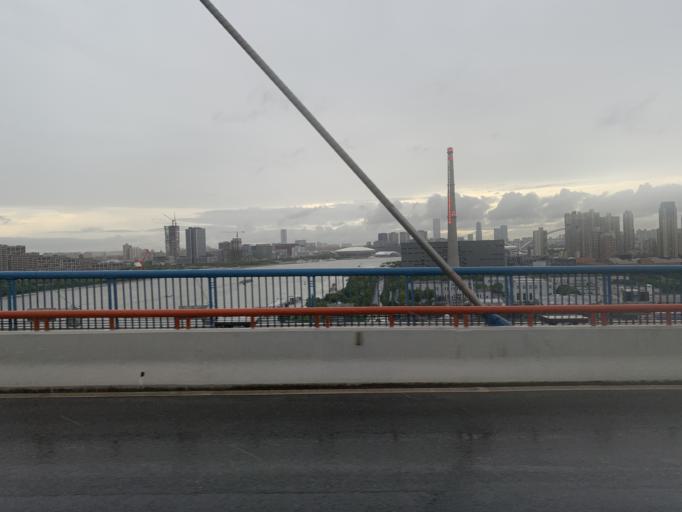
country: CN
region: Shanghai Shi
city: Luwan
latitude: 31.2084
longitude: 121.4983
